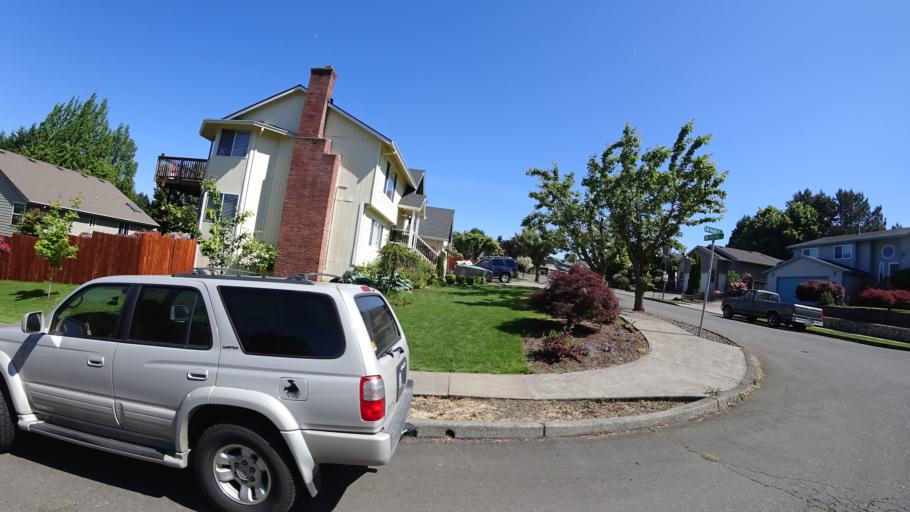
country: US
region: Oregon
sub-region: Multnomah County
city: Gresham
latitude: 45.4845
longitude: -122.4714
